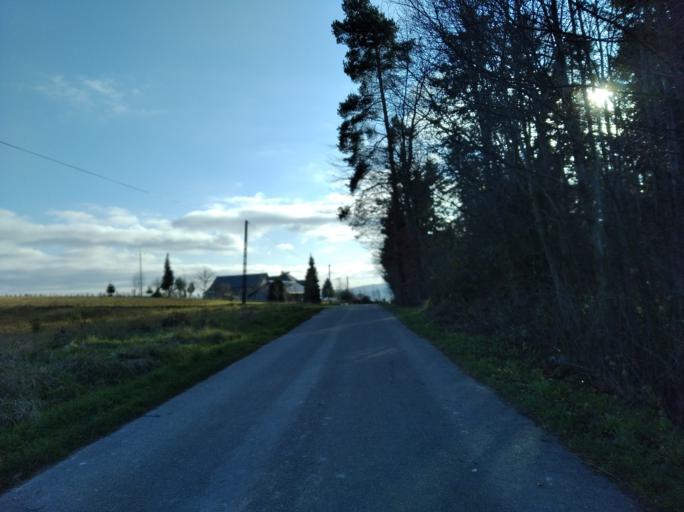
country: PL
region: Subcarpathian Voivodeship
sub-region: Powiat strzyzowski
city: Babica
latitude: 49.9112
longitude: 21.8486
